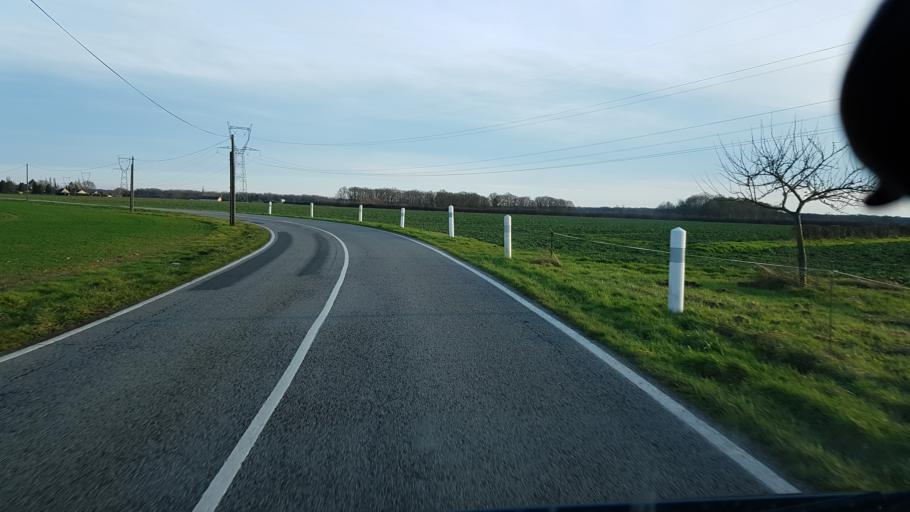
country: FR
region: Ile-de-France
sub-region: Departement des Yvelines
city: Auffargis
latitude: 48.6784
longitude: 1.9033
